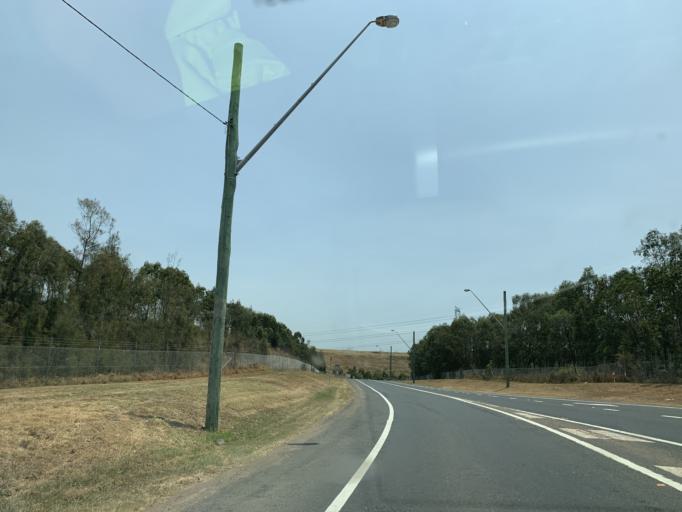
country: AU
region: New South Wales
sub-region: Fairfield
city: Horsley Park
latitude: -33.8167
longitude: 150.8674
